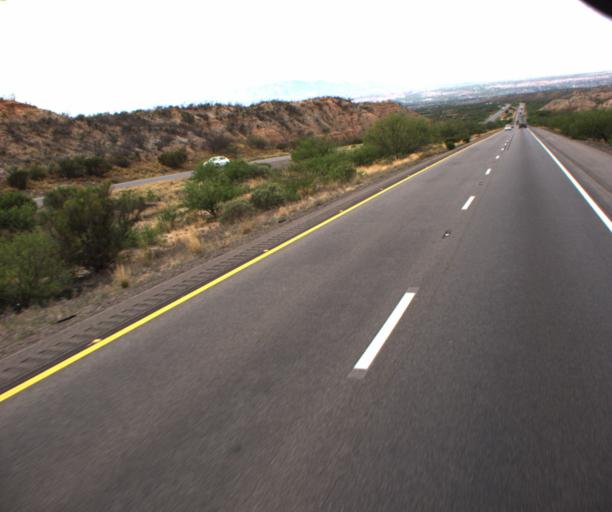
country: US
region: Arizona
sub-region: Cochise County
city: Saint David
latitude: 31.9825
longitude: -110.2091
